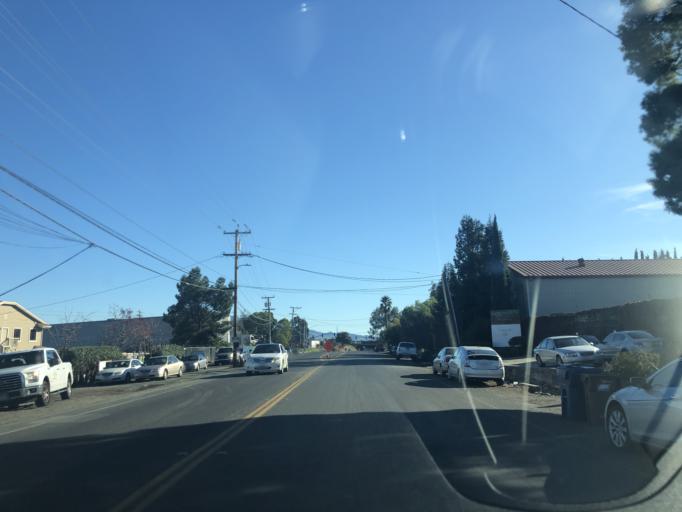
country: US
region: California
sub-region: Contra Costa County
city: Pacheco
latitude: 37.9962
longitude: -122.0761
